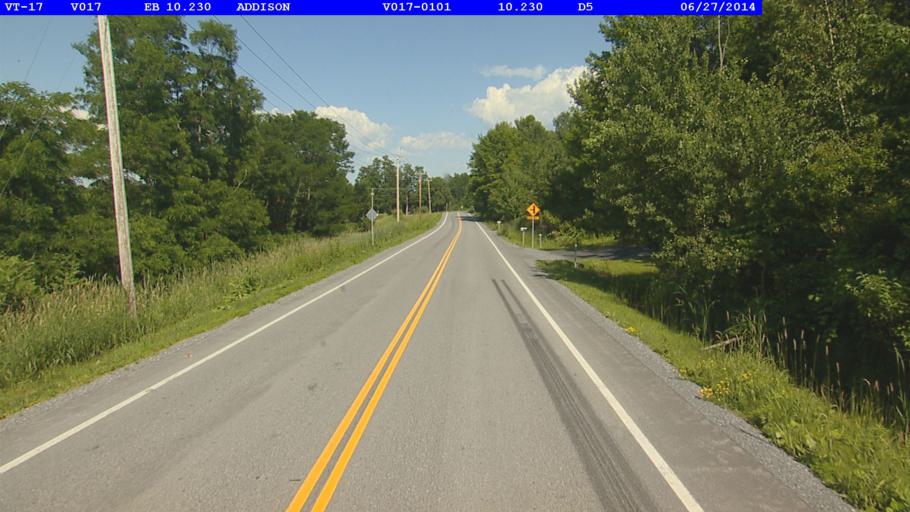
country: US
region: Vermont
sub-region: Addison County
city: Vergennes
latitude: 44.0823
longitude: -73.2680
